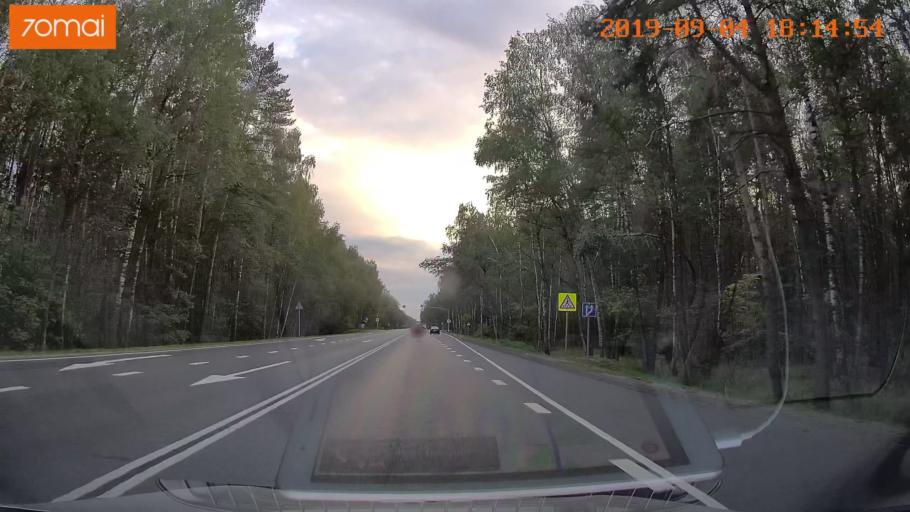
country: RU
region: Moskovskaya
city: Lopatinskiy
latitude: 55.3499
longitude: 38.7131
